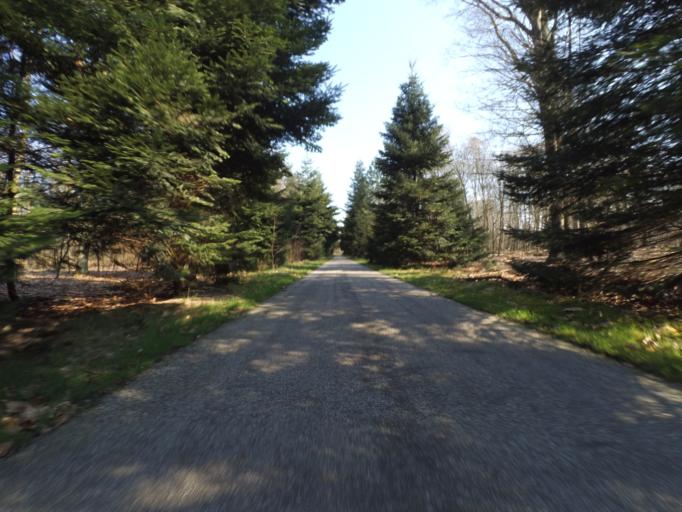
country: NL
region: Gelderland
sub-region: Gemeente Arnhem
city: Hoogkamp
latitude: 52.0354
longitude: 5.8658
